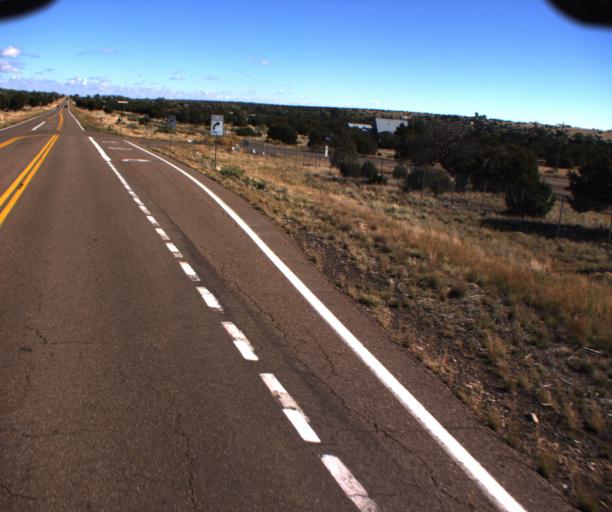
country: US
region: Arizona
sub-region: Apache County
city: Saint Johns
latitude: 34.4230
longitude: -109.6415
